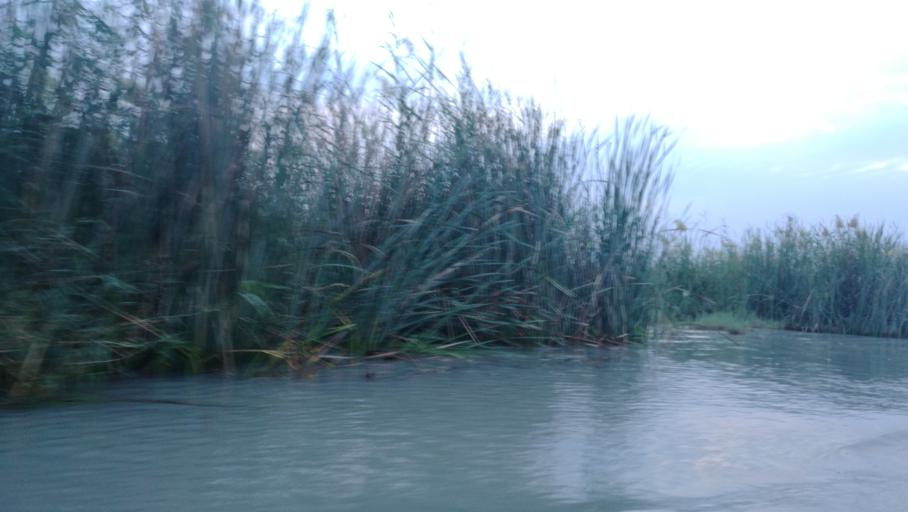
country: IQ
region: Dhi Qar
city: Al Jabayish
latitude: 30.9848
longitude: 47.0386
